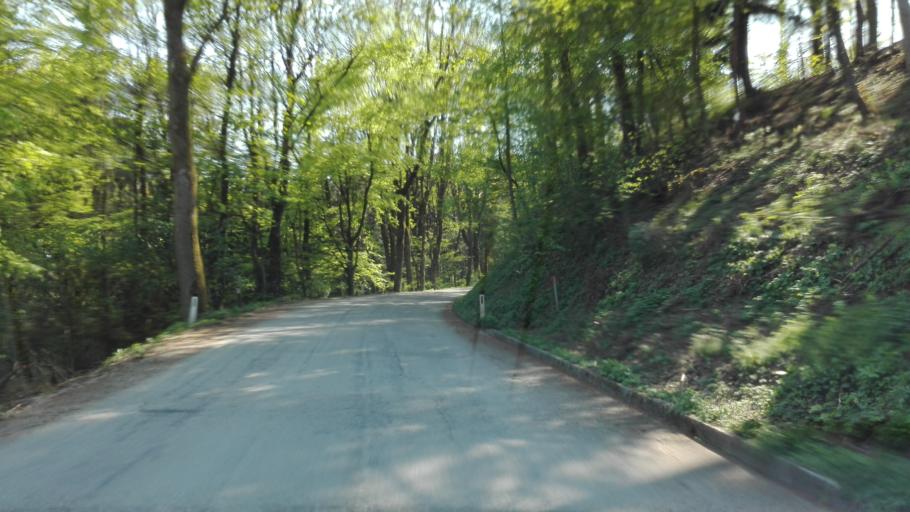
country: AT
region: Upper Austria
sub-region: Politischer Bezirk Rohrbach
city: Atzesberg
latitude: 48.4216
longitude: 13.9177
